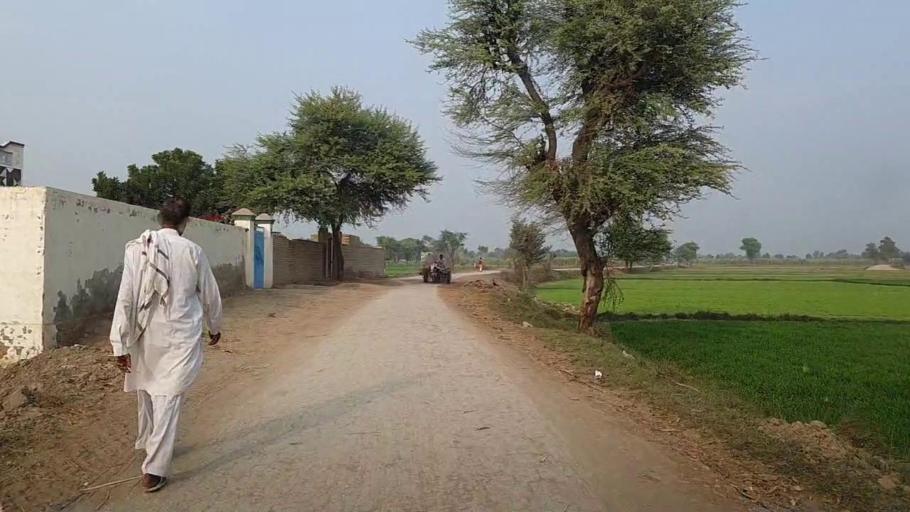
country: PK
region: Sindh
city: Setharja Old
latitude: 27.0921
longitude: 68.4983
